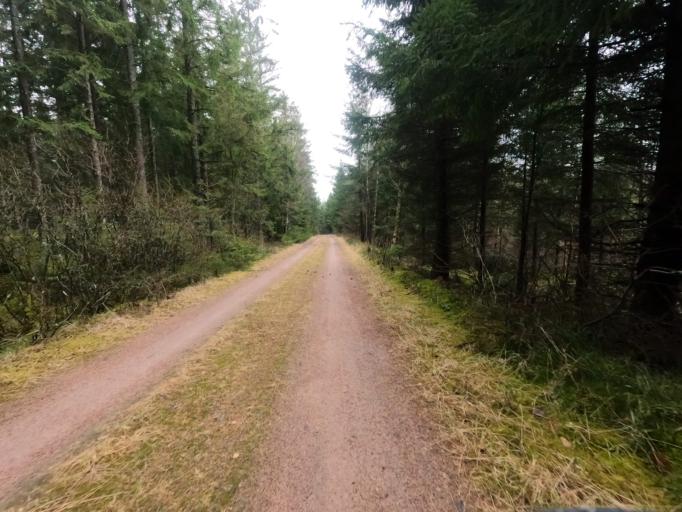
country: SE
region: Kronoberg
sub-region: Markaryds Kommun
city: Stromsnasbruk
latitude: 56.8053
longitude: 13.5698
